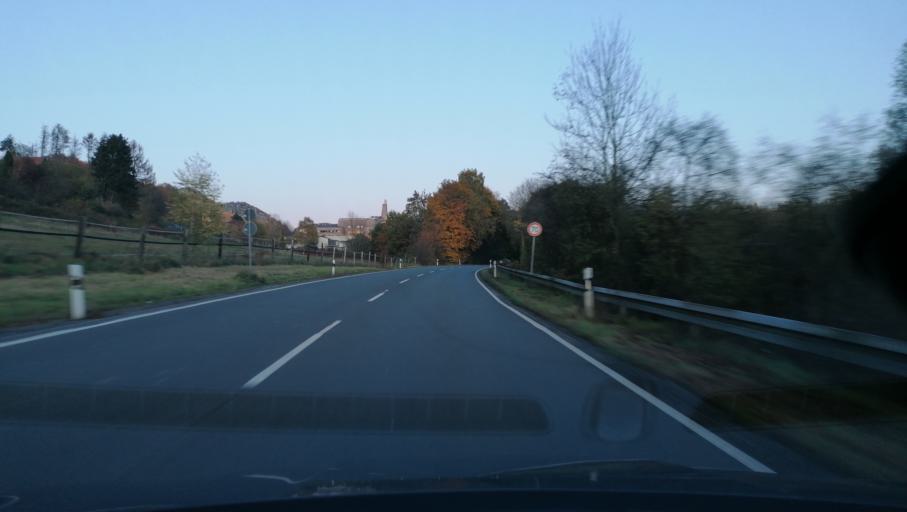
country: DE
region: North Rhine-Westphalia
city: Wetter (Ruhr)
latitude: 51.4088
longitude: 7.3930
